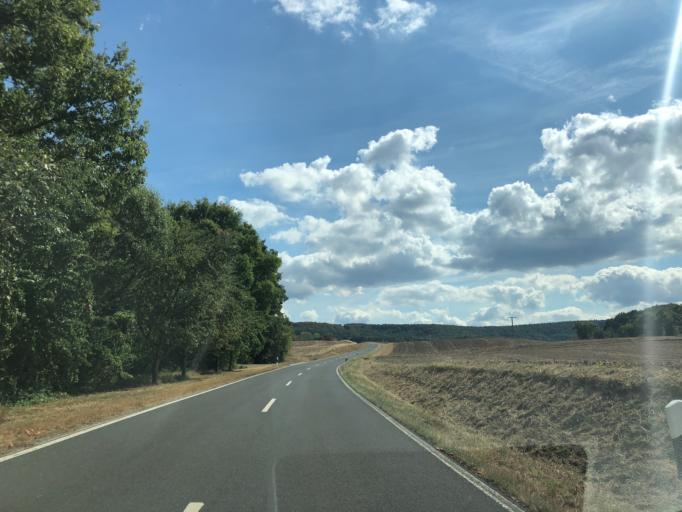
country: DE
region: Bavaria
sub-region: Regierungsbezirk Unterfranken
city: Oberschwarzach
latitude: 49.8392
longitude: 10.4333
